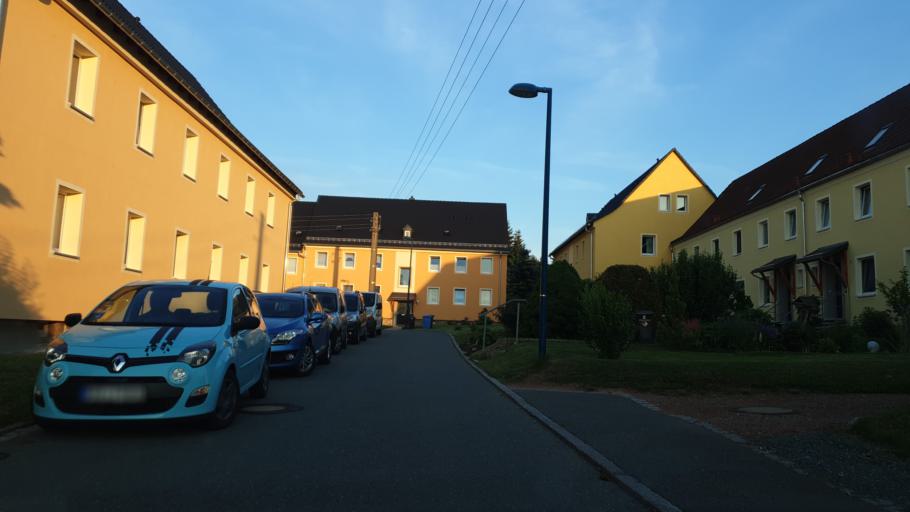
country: DE
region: Saxony
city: Oelsnitz
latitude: 50.7076
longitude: 12.7083
